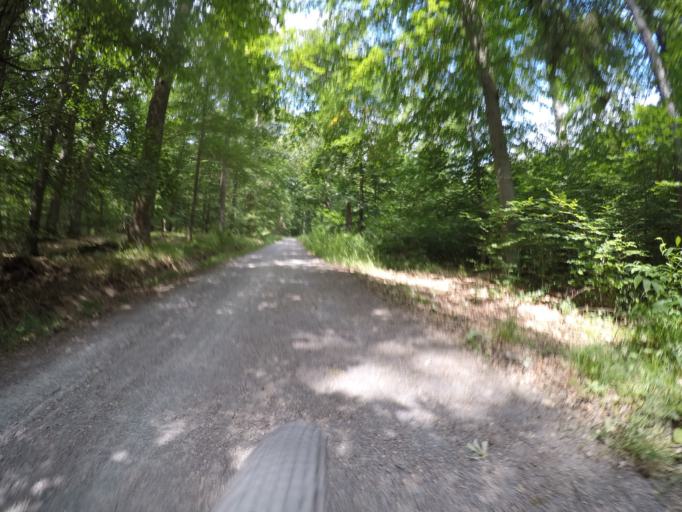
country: DE
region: Baden-Wuerttemberg
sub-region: Regierungsbezirk Stuttgart
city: Stuttgart Feuerbach
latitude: 48.7885
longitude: 9.1223
